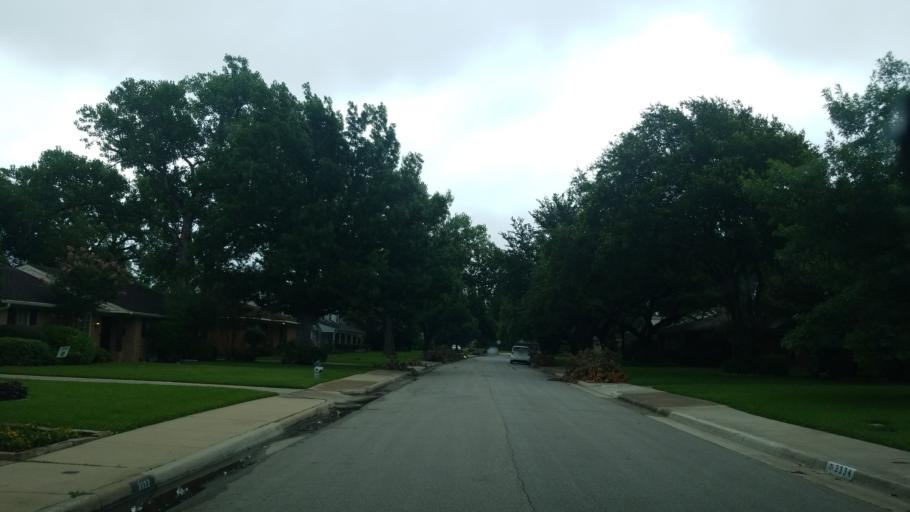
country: US
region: Texas
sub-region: Dallas County
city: Farmers Branch
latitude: 32.8941
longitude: -96.8667
